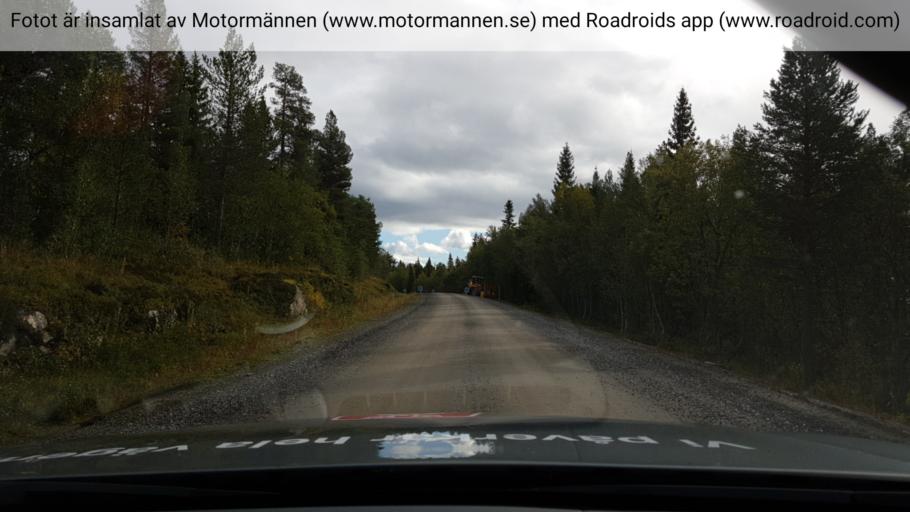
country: NO
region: Nord-Trondelag
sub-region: Snasa
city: Snaase
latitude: 63.7371
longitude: 12.4970
